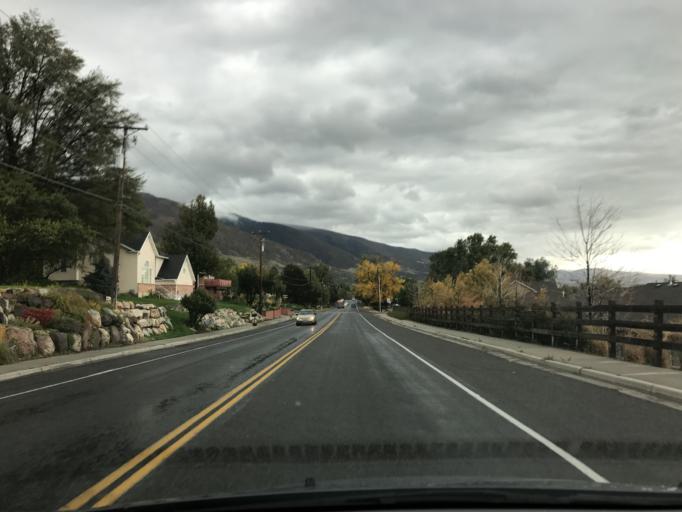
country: US
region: Utah
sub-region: Davis County
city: Fruit Heights
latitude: 41.0069
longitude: -111.9067
